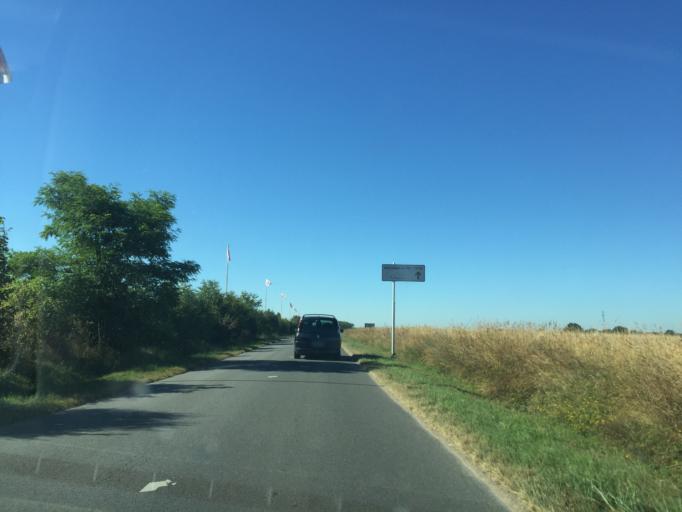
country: FR
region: Auvergne
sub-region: Departement de l'Allier
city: Dompierre-sur-Besbre
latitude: 46.5130
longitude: 3.6225
